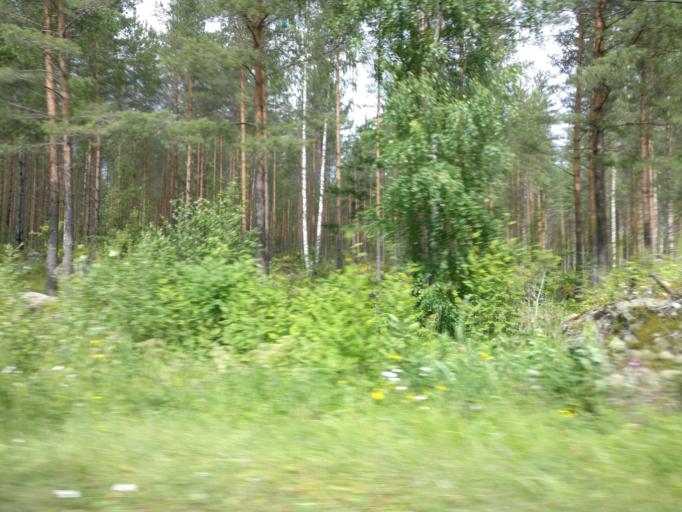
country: FI
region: Southern Savonia
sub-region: Pieksaemaeki
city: Joroinen
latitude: 62.1992
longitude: 28.0073
